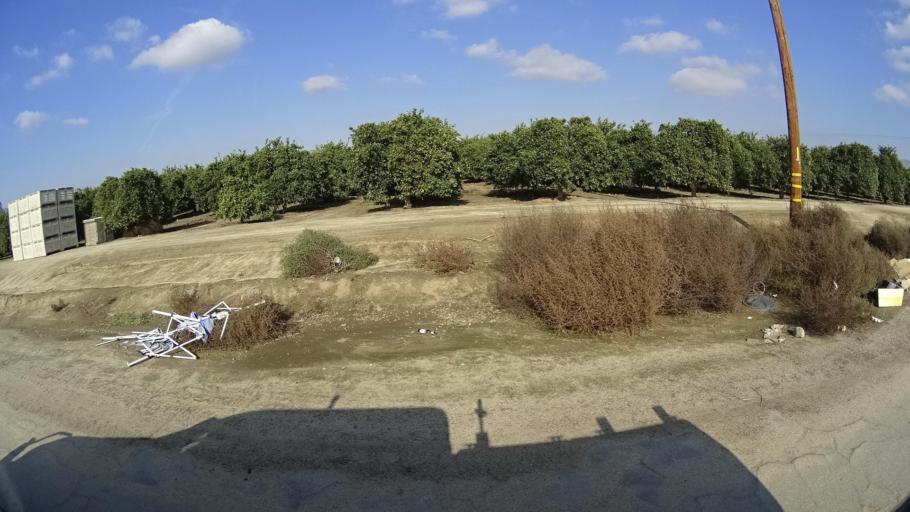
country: US
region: California
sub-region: Kern County
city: Arvin
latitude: 35.2385
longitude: -118.7713
